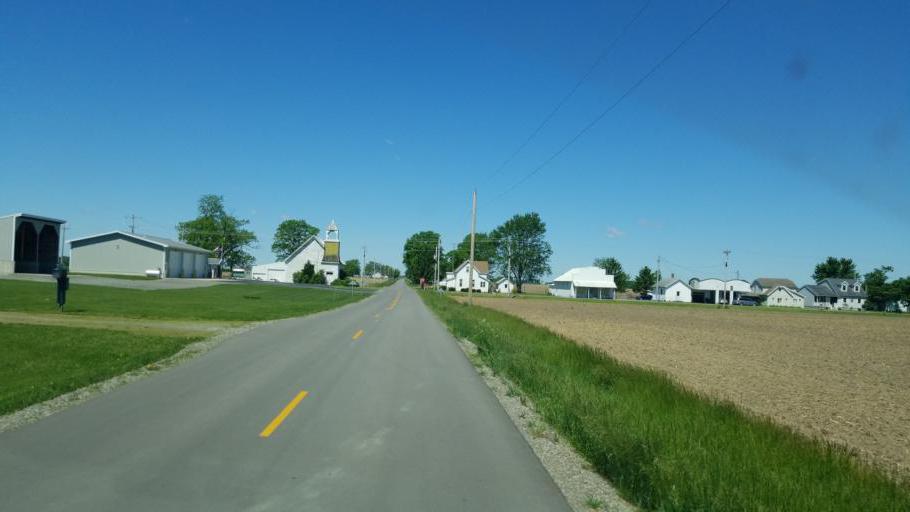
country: US
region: Ohio
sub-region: Logan County
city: Lakeview
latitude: 40.4174
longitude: -83.9443
